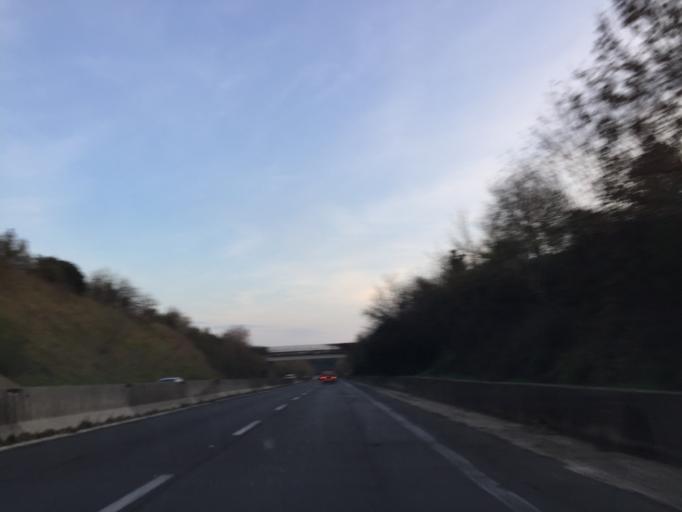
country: IT
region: Latium
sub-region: Citta metropolitana di Roma Capitale
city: Formello
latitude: 42.0209
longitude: 12.4339
